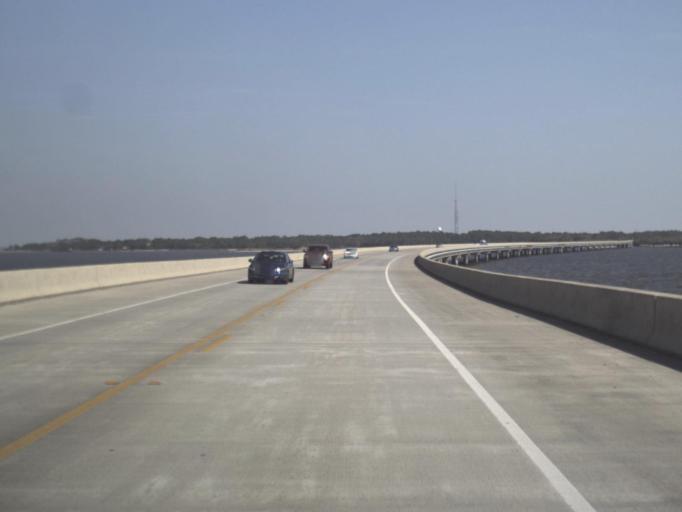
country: US
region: Florida
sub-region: Franklin County
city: Eastpoint
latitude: 29.7114
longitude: -84.8909
